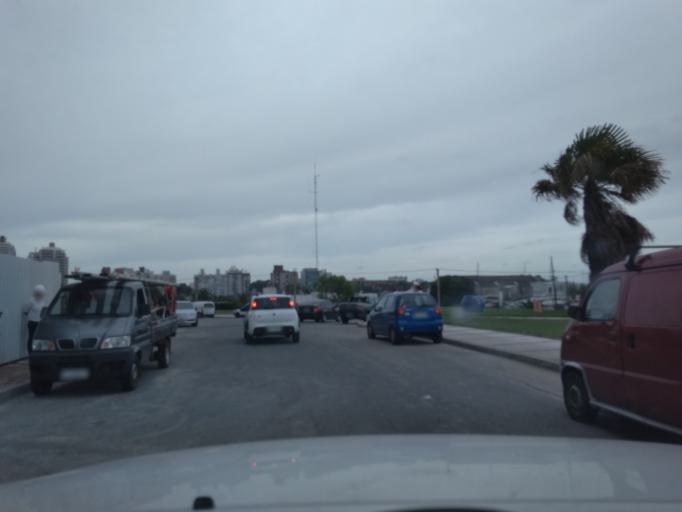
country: UY
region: Montevideo
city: Montevideo
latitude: -34.9102
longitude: -56.1334
